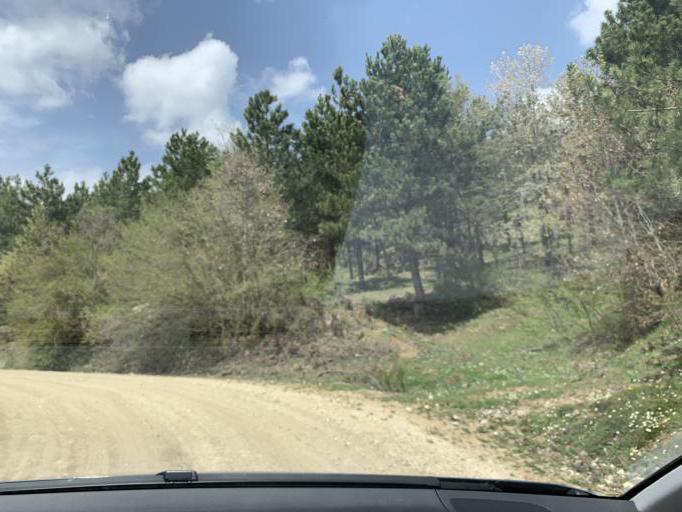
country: TR
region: Bolu
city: Bolu
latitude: 40.8326
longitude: 31.6733
